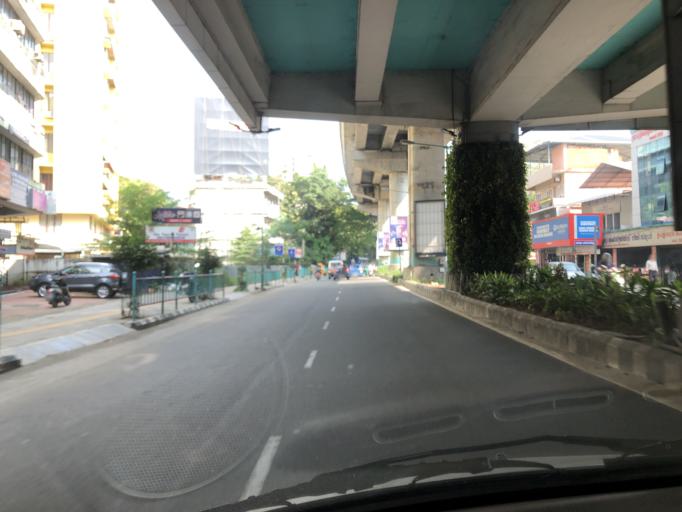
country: IN
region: Kerala
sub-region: Ernakulam
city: Elur
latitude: 10.0153
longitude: 76.3024
